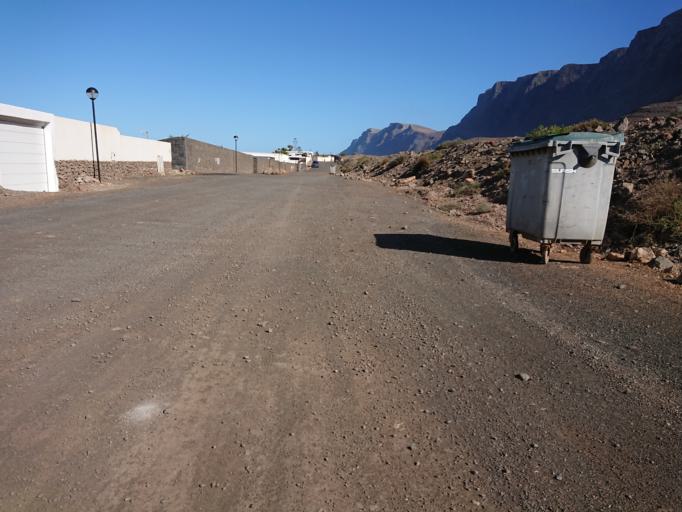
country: ES
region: Canary Islands
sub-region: Provincia de Las Palmas
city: Teguise
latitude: 29.1118
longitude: -13.5453
